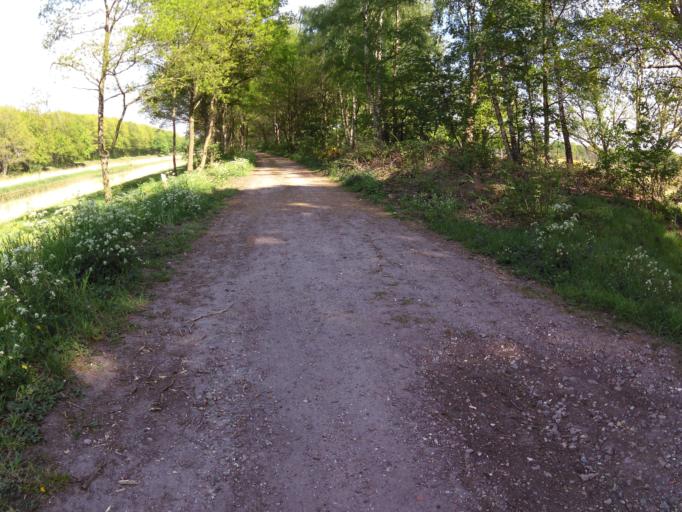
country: NL
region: North Brabant
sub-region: Gemeente Vught
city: Vught
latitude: 51.6697
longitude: 5.2266
